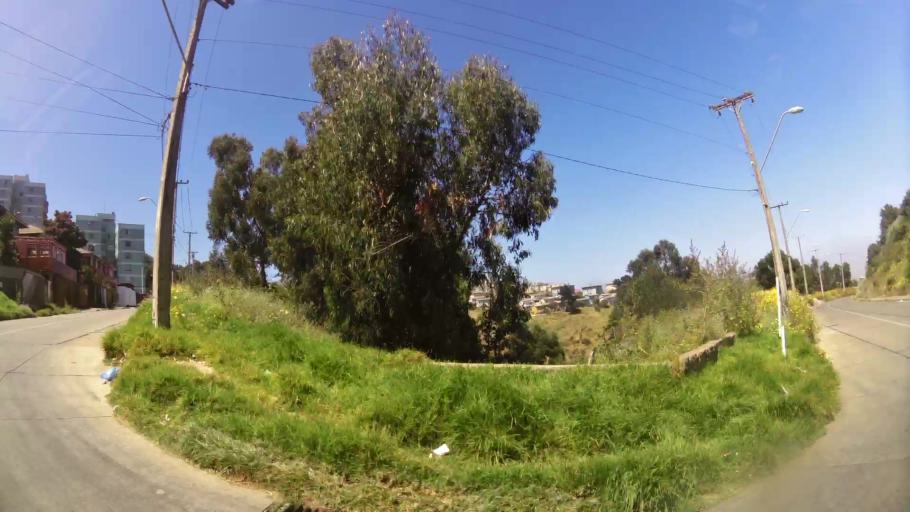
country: CL
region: Valparaiso
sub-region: Provincia de Valparaiso
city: Valparaiso
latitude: -33.0378
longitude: -71.6488
